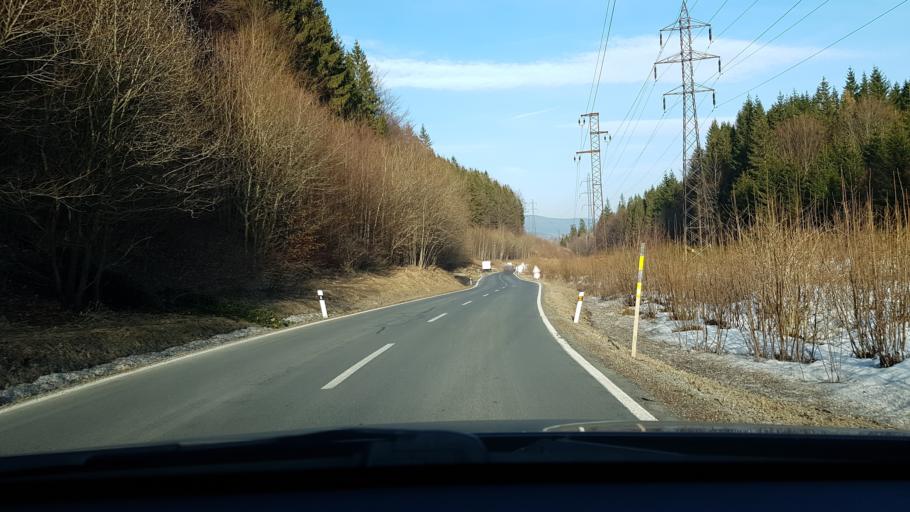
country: CZ
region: Olomoucky
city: Vapenna
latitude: 50.2070
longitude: 17.0856
